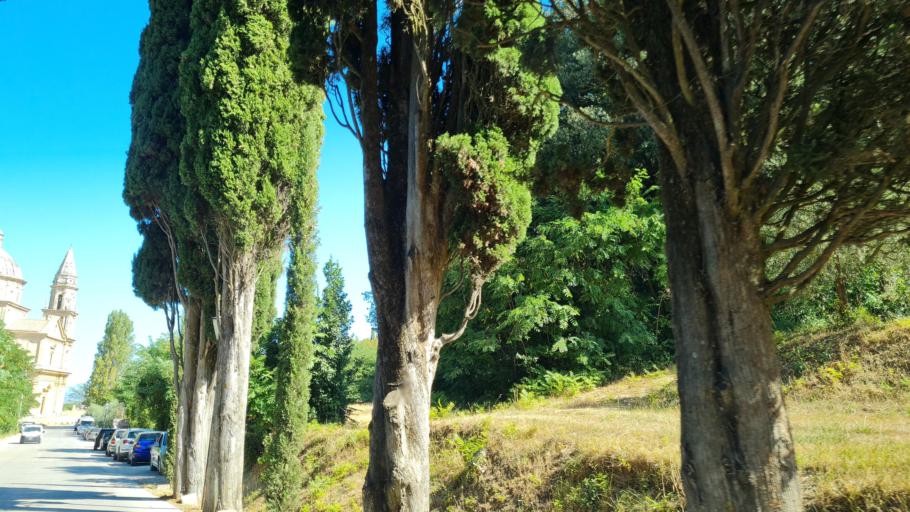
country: IT
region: Tuscany
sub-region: Provincia di Siena
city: Montepulciano
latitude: 43.0889
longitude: 11.7755
